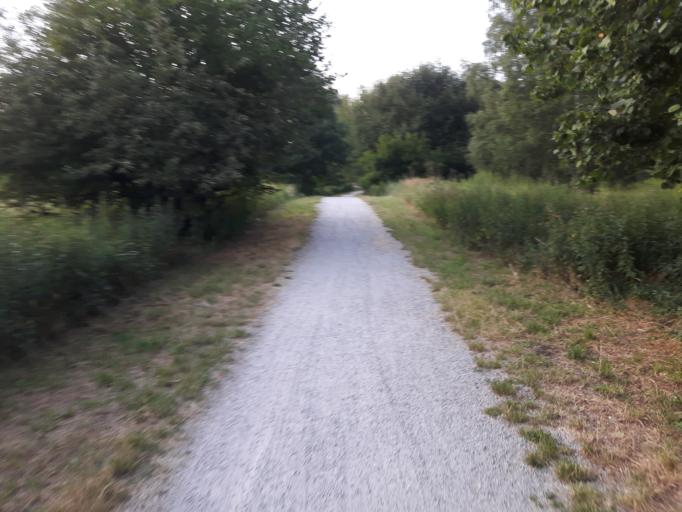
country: DE
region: Berlin
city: Staaken
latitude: 52.5526
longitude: 13.1386
